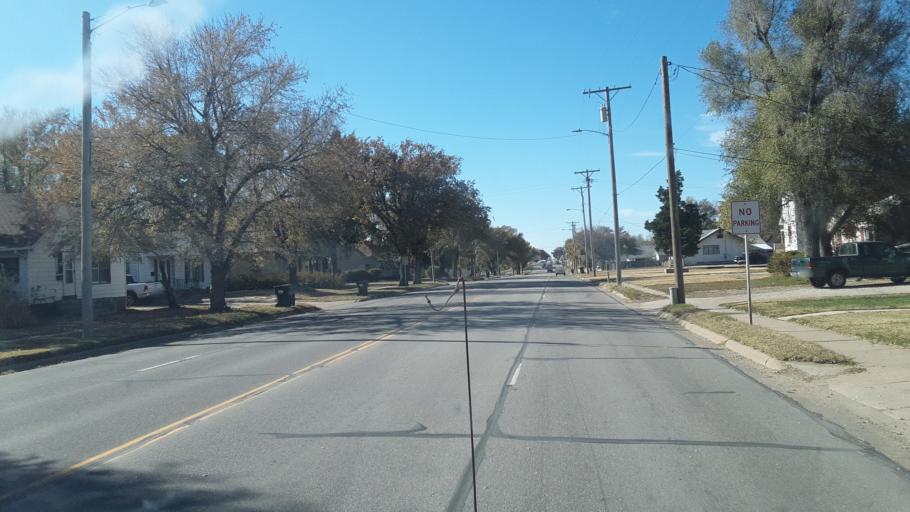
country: US
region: Kansas
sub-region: Rice County
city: Lyons
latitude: 38.3477
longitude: -98.1961
